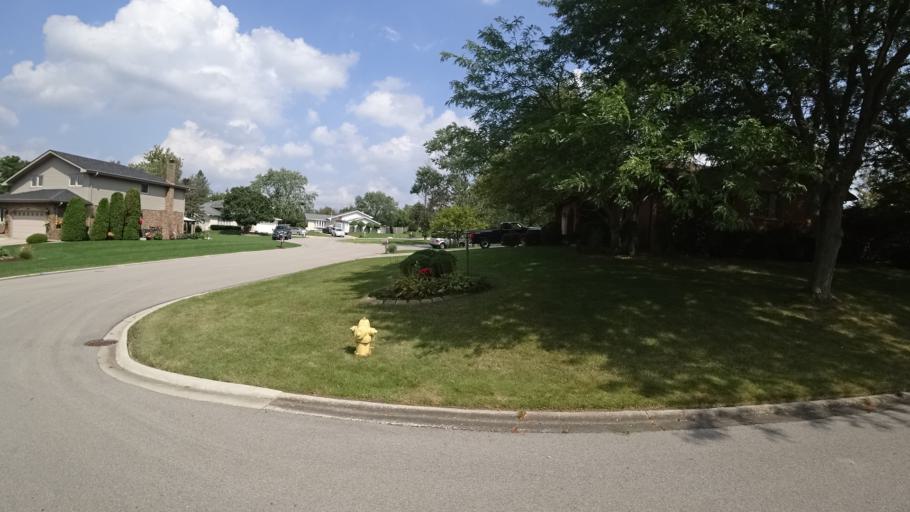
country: US
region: Illinois
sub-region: Will County
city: Goodings Grove
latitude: 41.6417
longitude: -87.9135
